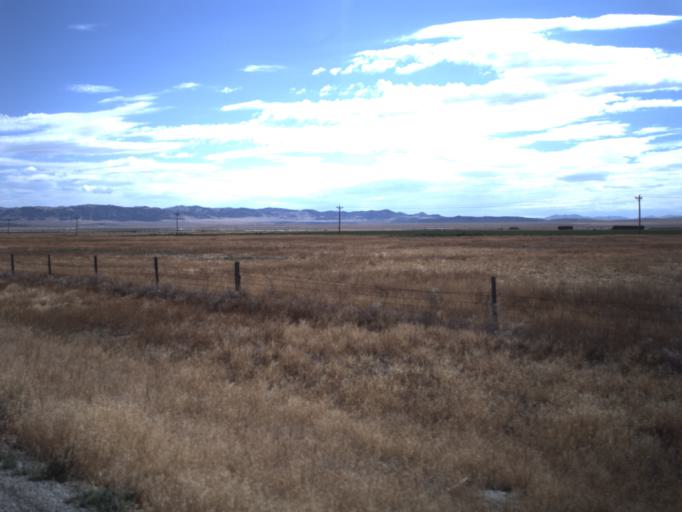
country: US
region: Idaho
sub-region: Oneida County
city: Malad City
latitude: 41.9665
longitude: -112.9194
